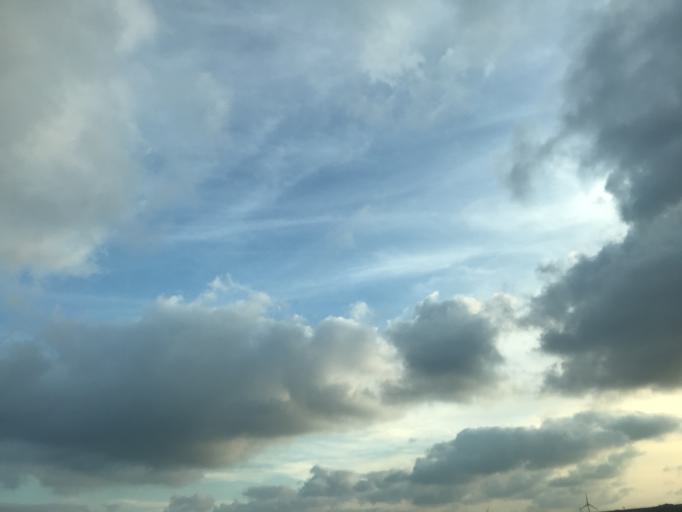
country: TR
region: Istanbul
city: Durusu
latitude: 41.2621
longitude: 28.7138
